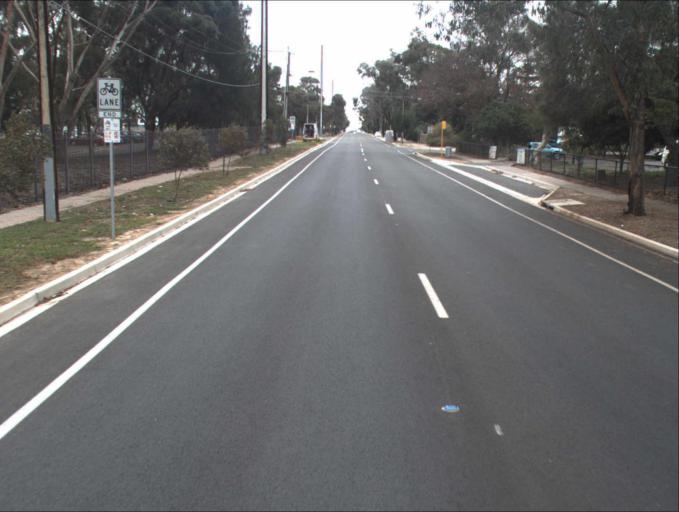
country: AU
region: South Australia
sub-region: Port Adelaide Enfield
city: Gilles Plains
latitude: -34.8522
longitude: 138.6537
